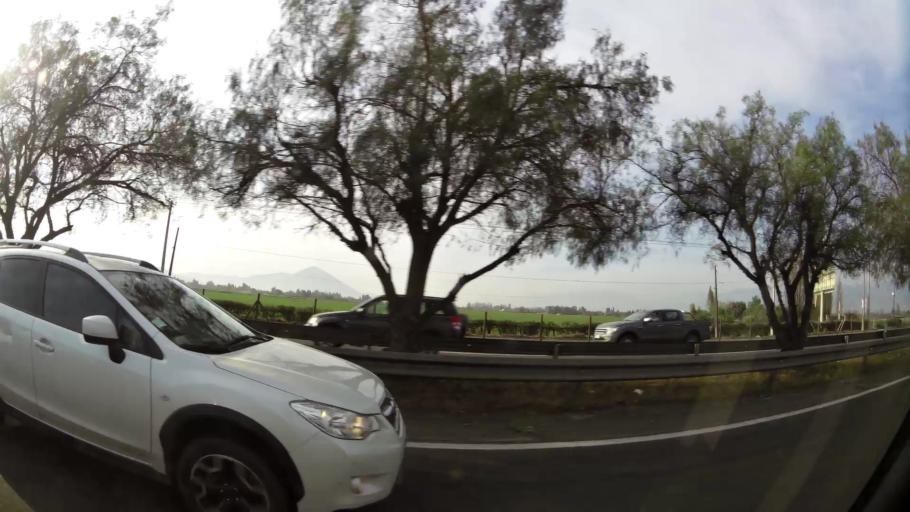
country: CL
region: Santiago Metropolitan
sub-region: Provincia de Talagante
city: Talagante
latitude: -33.6613
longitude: -70.9012
